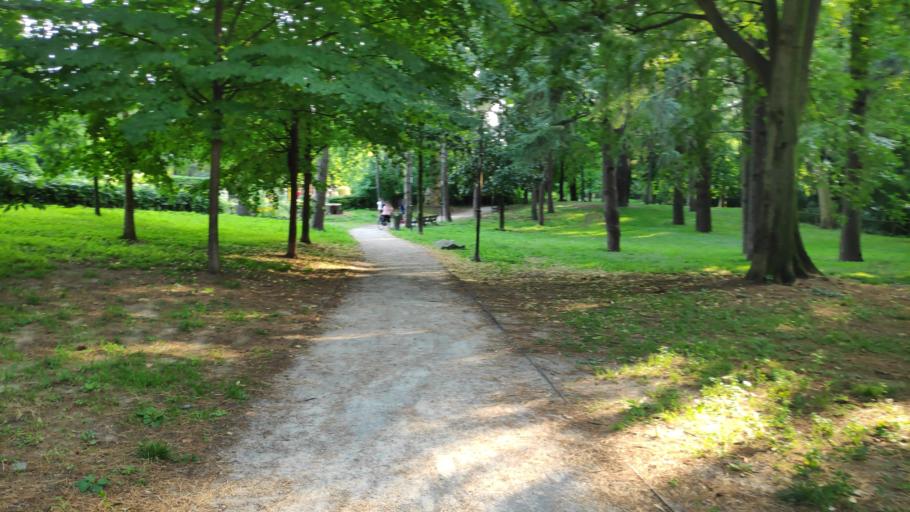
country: IT
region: Lombardy
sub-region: Citta metropolitana di Milano
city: Cernusco sul Naviglio
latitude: 45.5224
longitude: 9.3297
